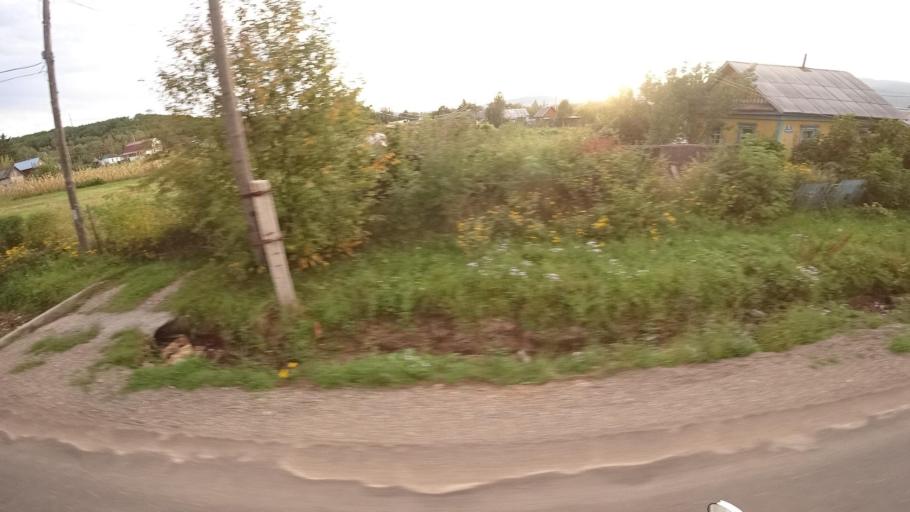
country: RU
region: Primorskiy
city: Yakovlevka
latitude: 44.4226
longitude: 133.4664
